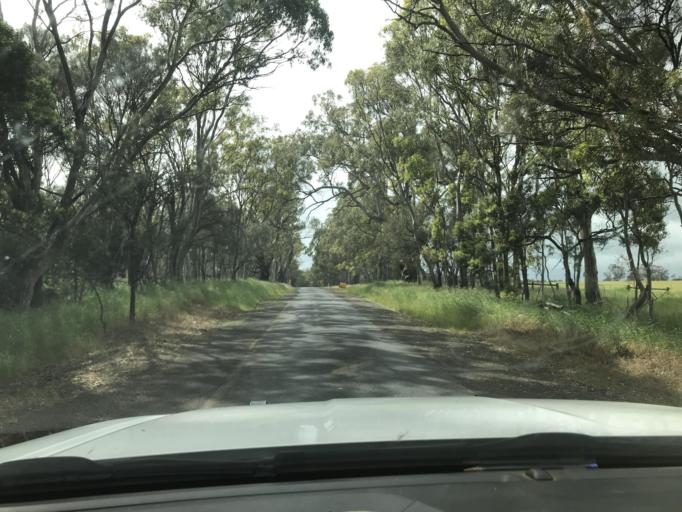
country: AU
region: South Australia
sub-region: Wattle Range
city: Penola
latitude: -37.1683
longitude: 141.4241
